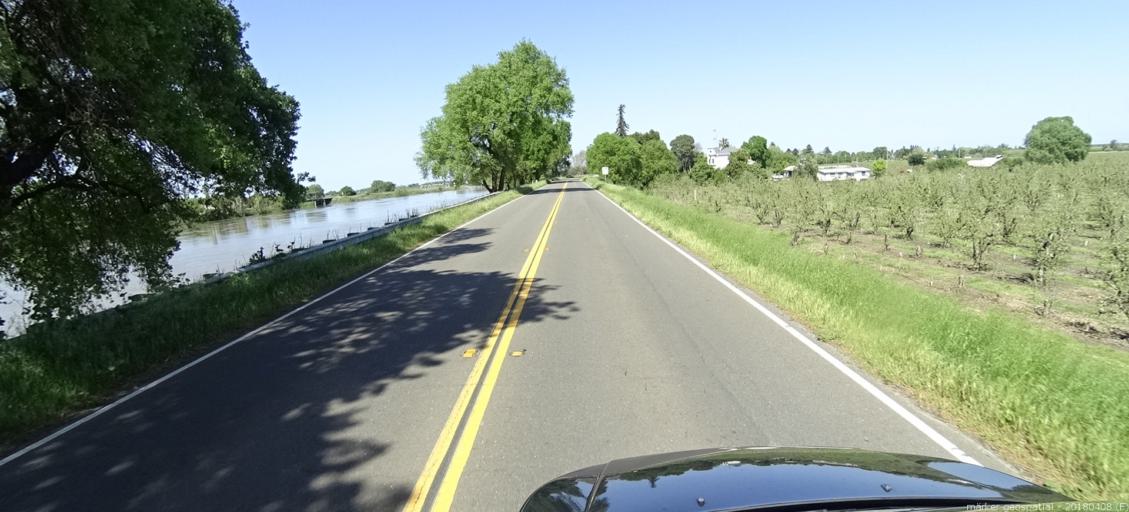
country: US
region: California
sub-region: Sacramento County
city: Walnut Grove
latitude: 38.3237
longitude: -121.5756
